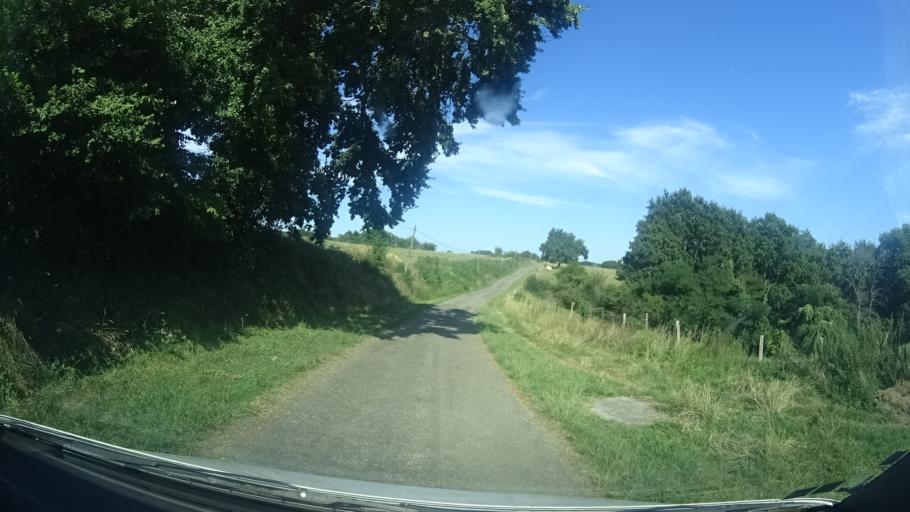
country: FR
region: Aquitaine
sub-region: Departement des Pyrenees-Atlantiques
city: Orthez
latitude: 43.5071
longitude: -0.7080
